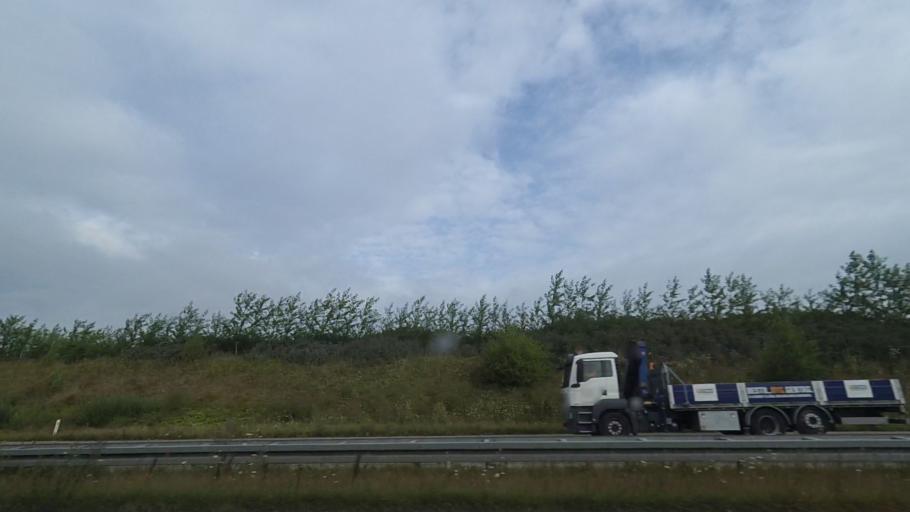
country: DK
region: Central Jutland
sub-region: Arhus Kommune
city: Hjortshoj
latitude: 56.2397
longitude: 10.2807
